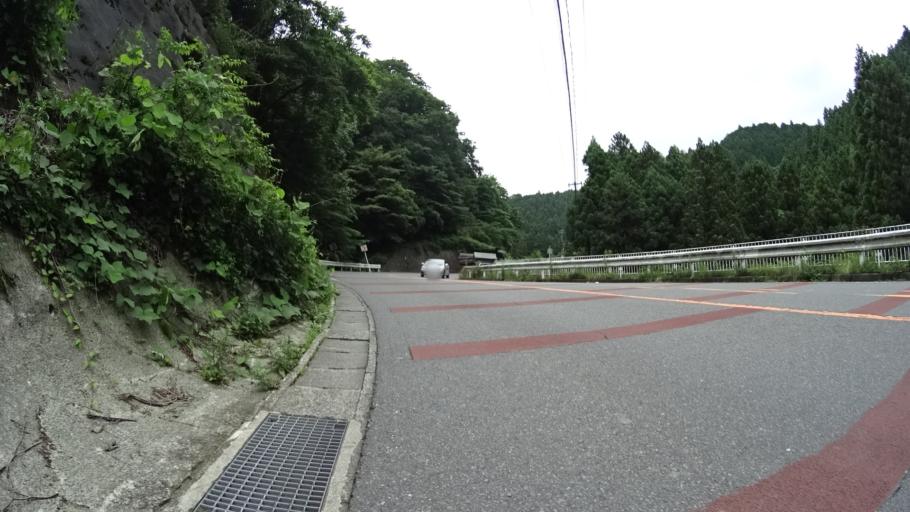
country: JP
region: Kanagawa
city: Atsugi
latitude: 35.5007
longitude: 139.2595
